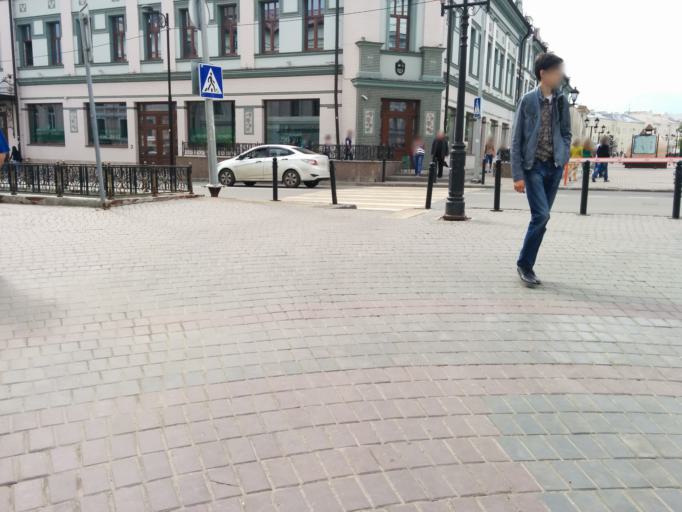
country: RU
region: Tatarstan
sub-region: Gorod Kazan'
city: Kazan
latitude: 55.7928
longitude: 49.1107
